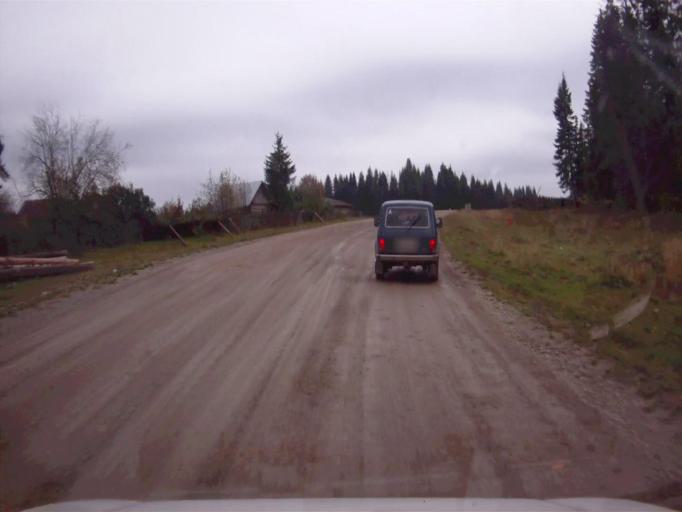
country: RU
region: Chelyabinsk
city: Nyazepetrovsk
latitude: 56.0616
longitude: 59.5642
